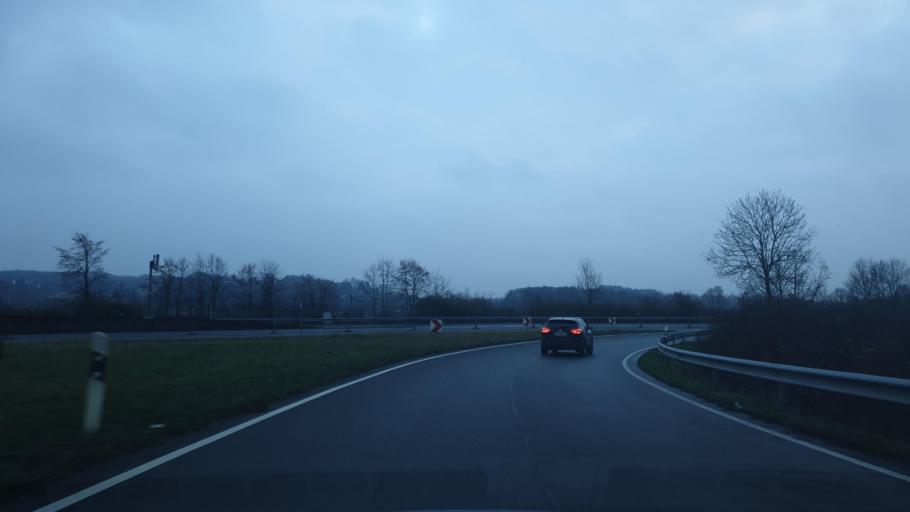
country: DE
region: North Rhine-Westphalia
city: Porta Westfalica
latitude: 52.2431
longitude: 8.9120
